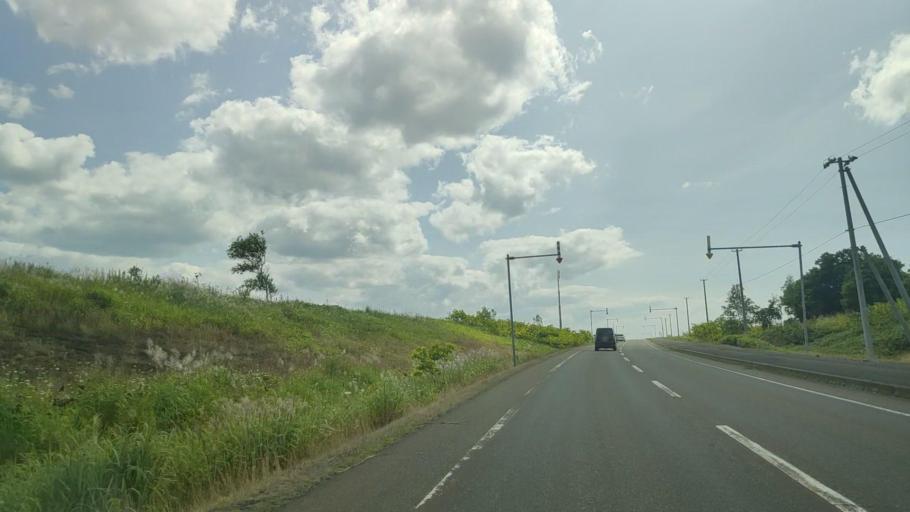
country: JP
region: Hokkaido
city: Makubetsu
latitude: 44.7904
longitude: 141.7904
